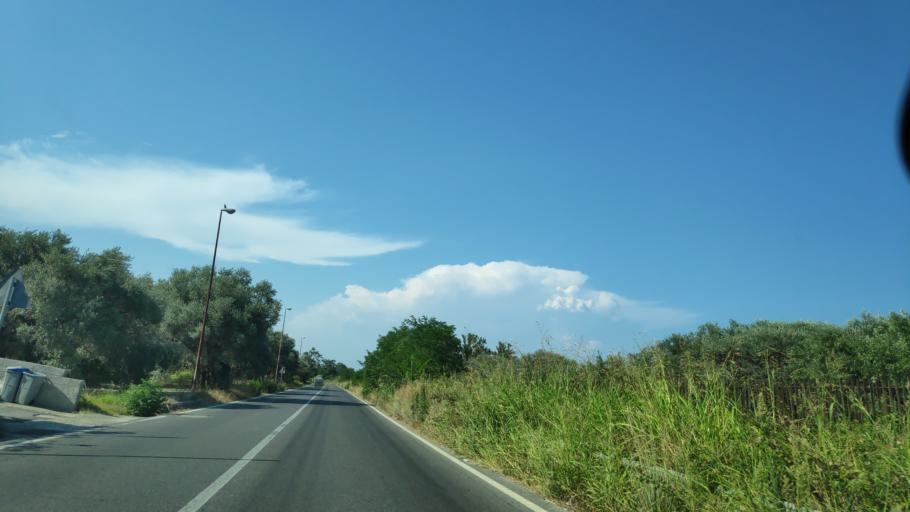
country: IT
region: Calabria
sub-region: Provincia di Catanzaro
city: Badolato Marina
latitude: 38.5857
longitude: 16.5638
